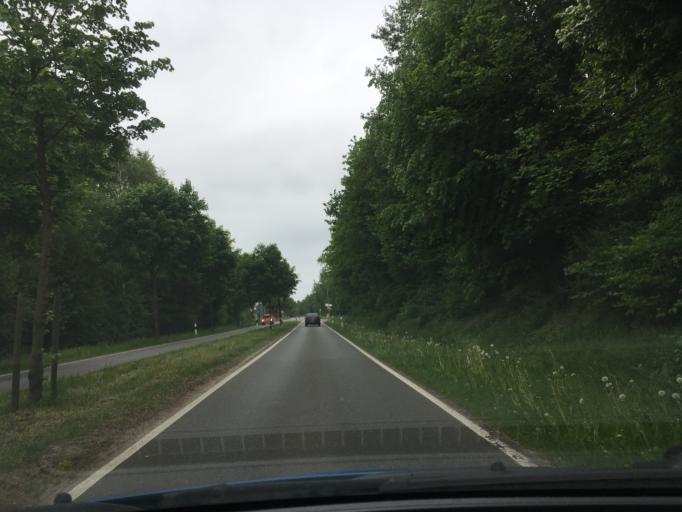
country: DE
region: Lower Saxony
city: Buchholz in der Nordheide
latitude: 53.3496
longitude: 9.8701
